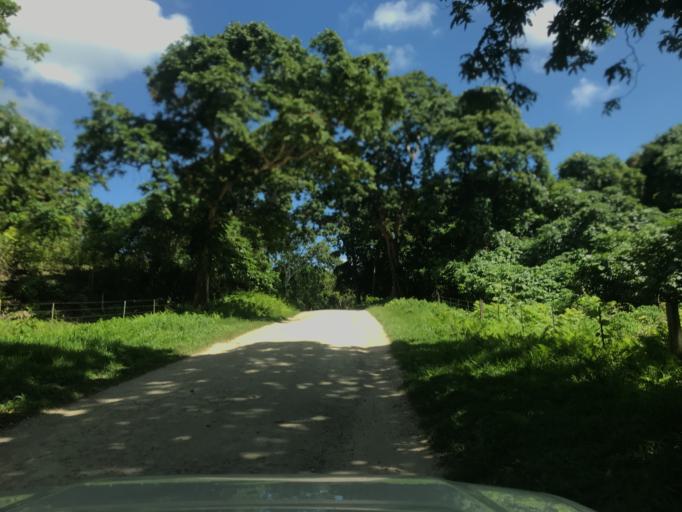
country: VU
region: Sanma
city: Luganville
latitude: -15.5787
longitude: 167.0336
